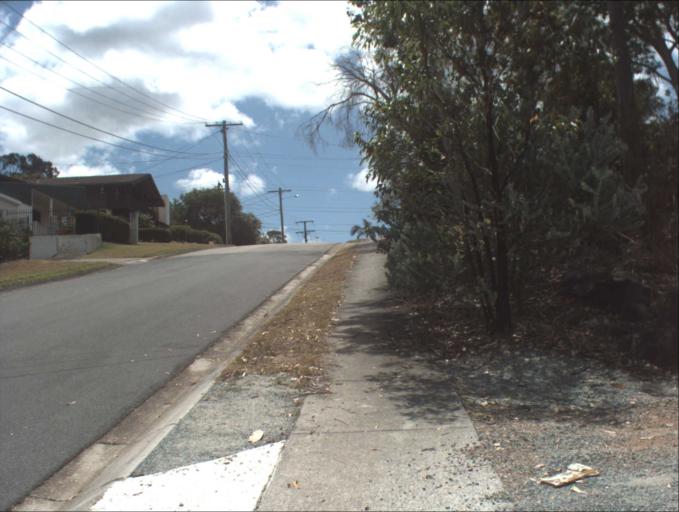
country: AU
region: Queensland
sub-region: Logan
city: Slacks Creek
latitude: -27.6524
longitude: 153.1713
